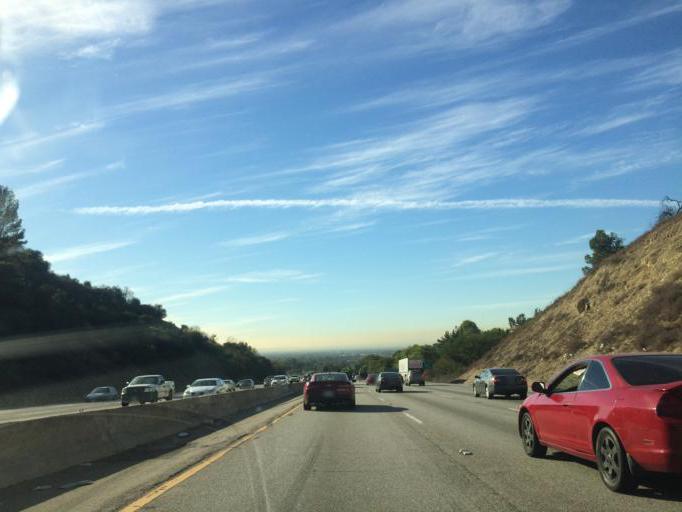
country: US
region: California
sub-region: Los Angeles County
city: Charter Oak
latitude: 34.0683
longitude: -117.8486
